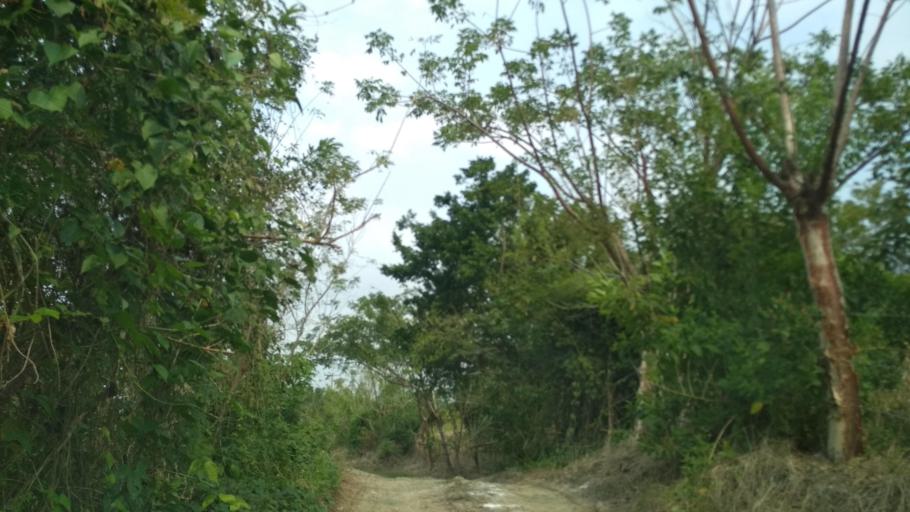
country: MM
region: Kayah
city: Loikaw
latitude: 20.2103
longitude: 97.3151
